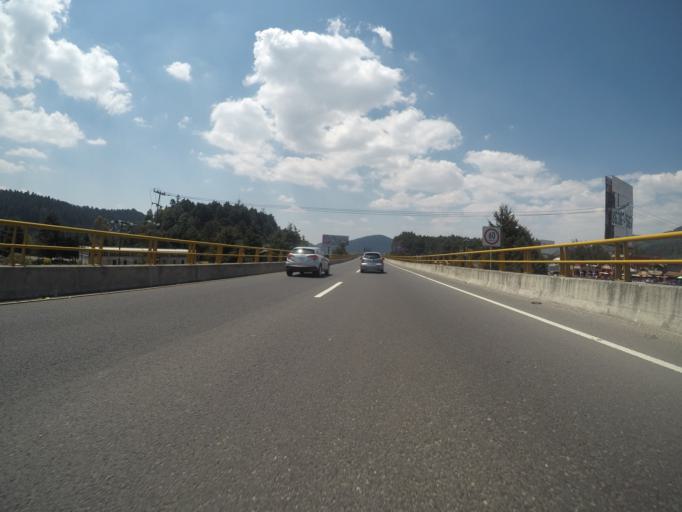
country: MX
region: Mexico
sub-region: Huixquilucan
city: El Palacio
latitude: 19.3006
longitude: -99.3731
